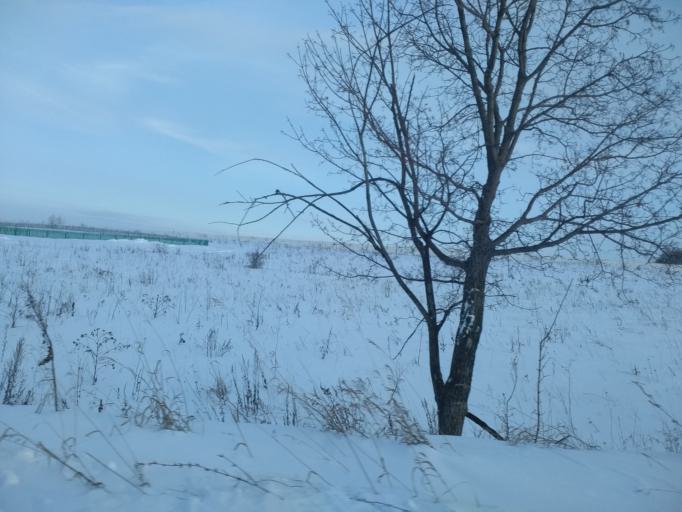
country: RU
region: Bashkortostan
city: Iglino
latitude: 54.7707
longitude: 56.5489
